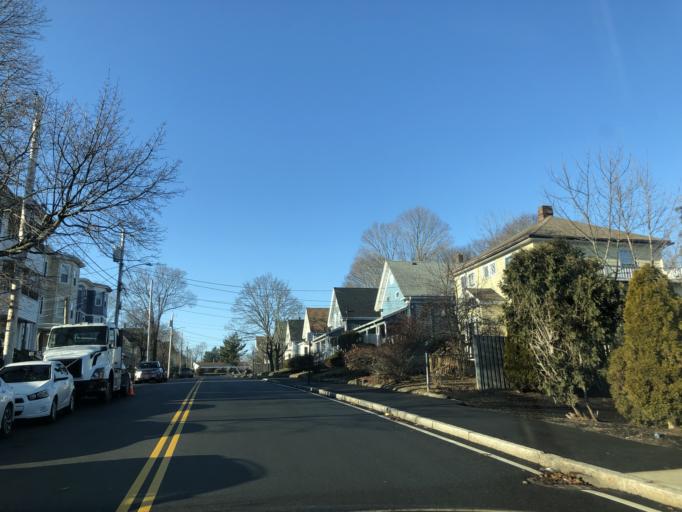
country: US
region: Massachusetts
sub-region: Plymouth County
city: Brockton
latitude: 42.1075
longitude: -71.0248
